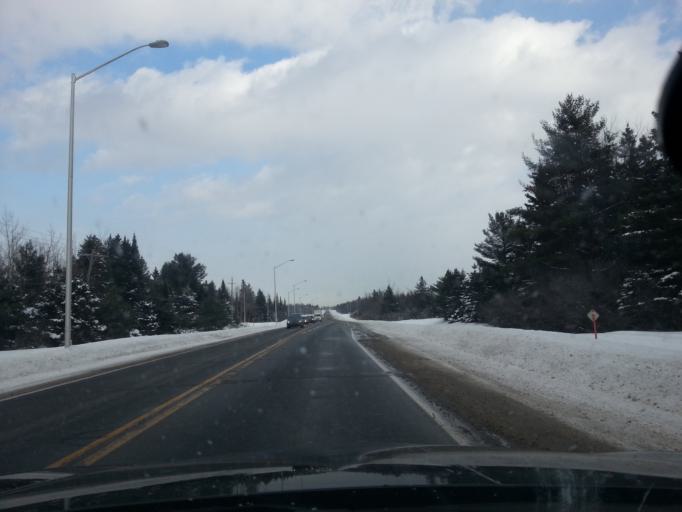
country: CA
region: Ontario
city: Bells Corners
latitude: 45.2519
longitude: -75.9613
